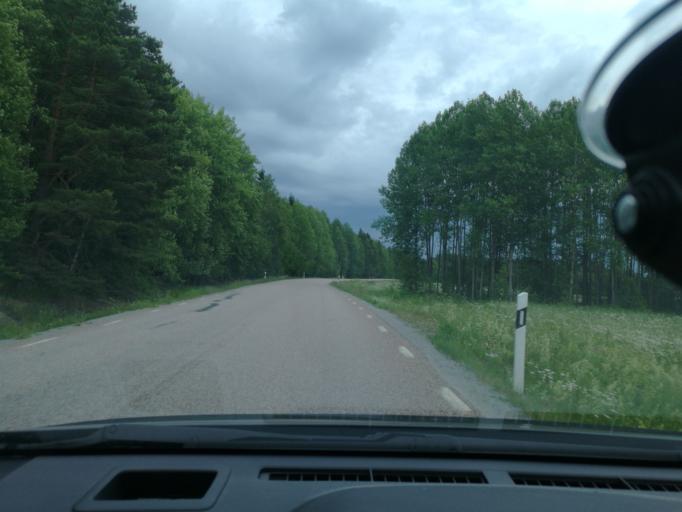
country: SE
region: Vaestmanland
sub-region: Sala Kommun
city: Sala
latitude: 59.9162
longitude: 16.4779
